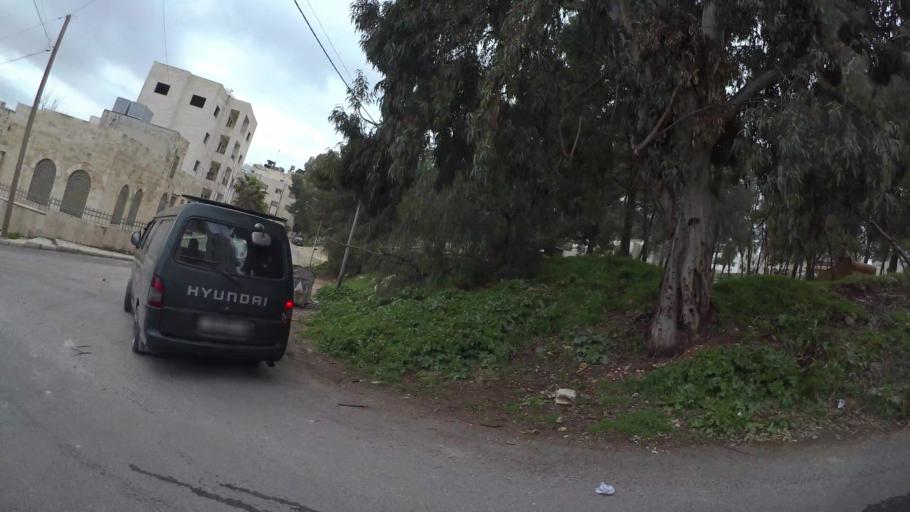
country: JO
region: Amman
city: Wadi as Sir
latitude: 31.9460
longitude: 35.8233
